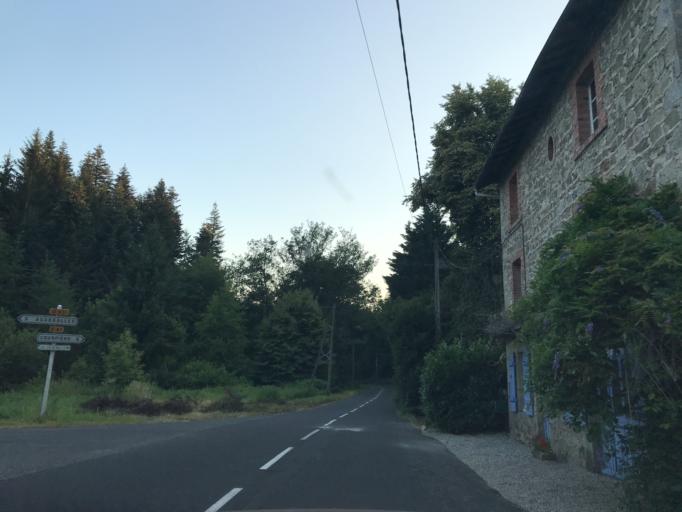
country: FR
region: Auvergne
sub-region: Departement du Puy-de-Dome
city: Courpiere
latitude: 45.7399
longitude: 3.6001
